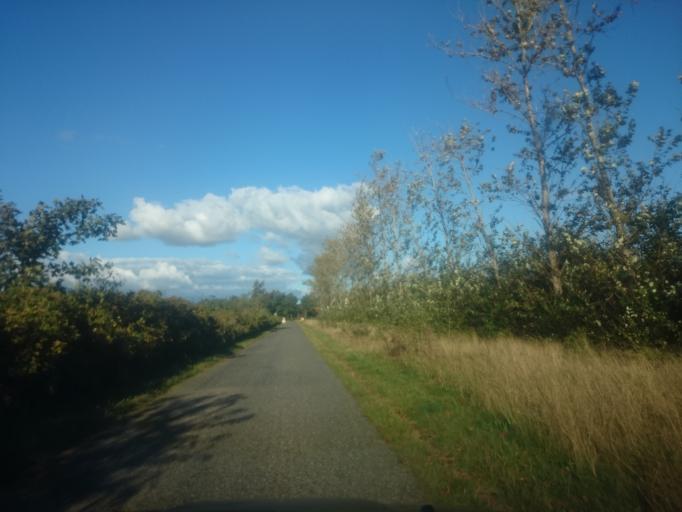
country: DK
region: South Denmark
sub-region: Billund Kommune
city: Billund
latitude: 55.7171
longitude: 9.1088
